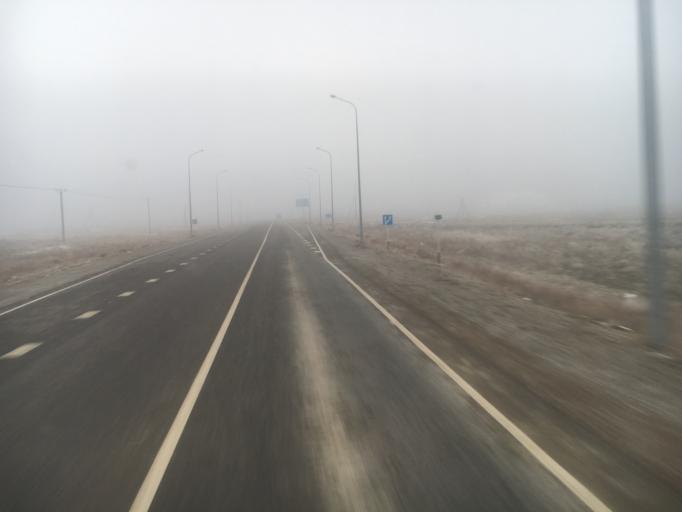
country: KZ
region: Zhambyl
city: Sarykemer
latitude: 43.0503
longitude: 71.4610
